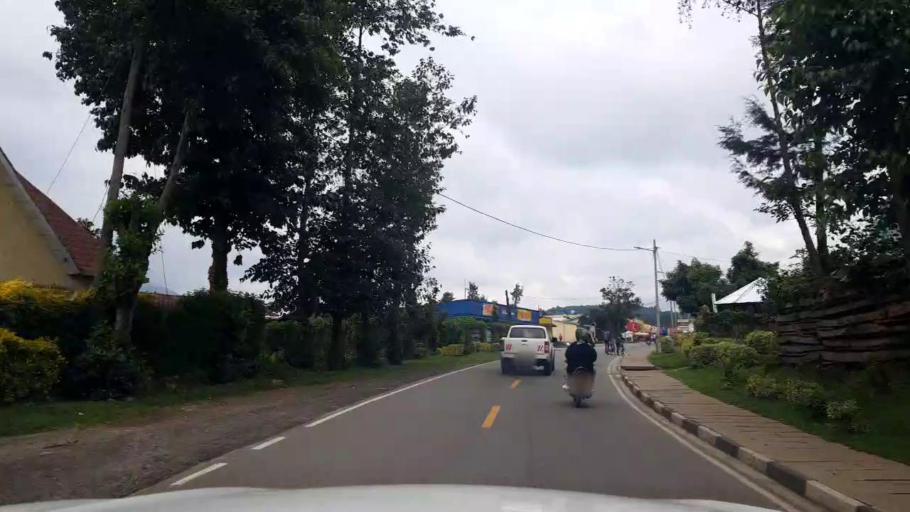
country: RW
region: Northern Province
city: Musanze
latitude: -1.4497
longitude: 29.5907
